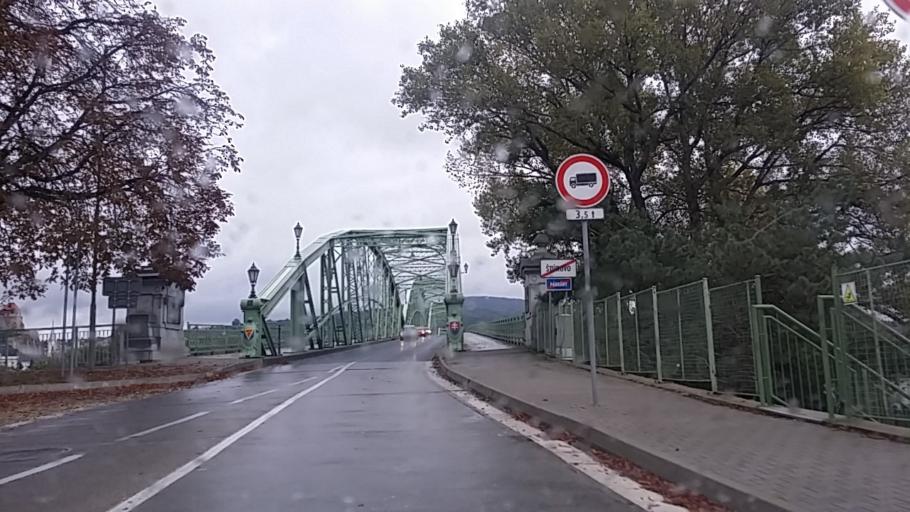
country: SK
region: Nitriansky
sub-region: Okres Nove Zamky
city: Sturovo
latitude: 47.7958
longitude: 18.7261
